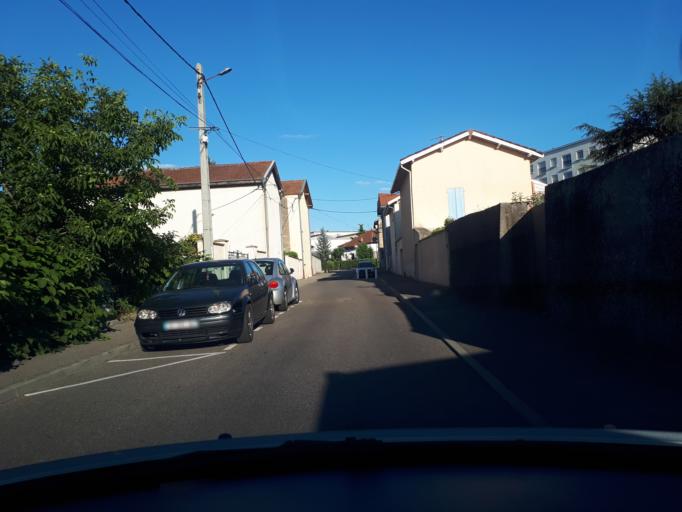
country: FR
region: Rhone-Alpes
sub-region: Departement de l'Isere
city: Bourgoin-Jallieu
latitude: 45.5913
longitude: 5.2678
